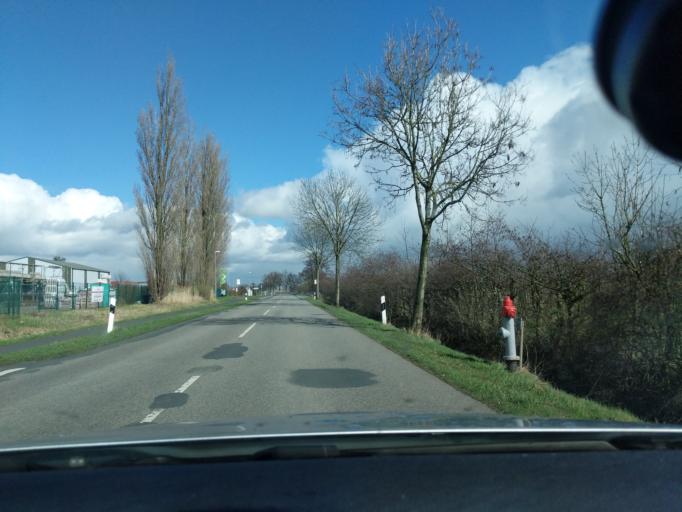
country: DE
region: Lower Saxony
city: Stade
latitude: 53.6062
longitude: 9.5201
